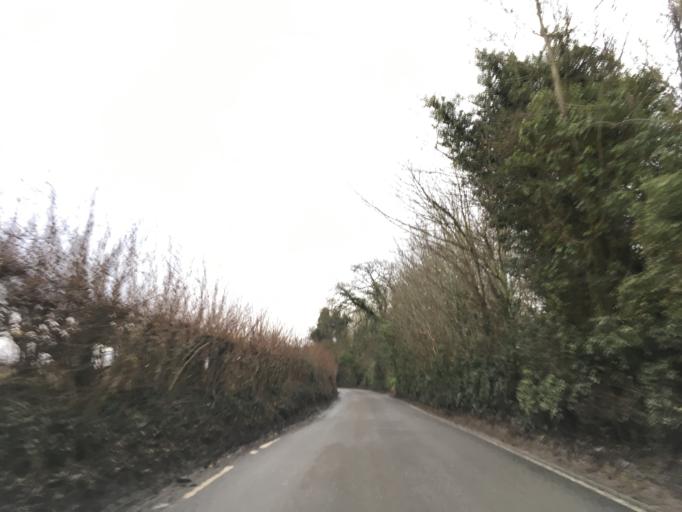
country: GB
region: England
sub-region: South Gloucestershire
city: Winterbourne
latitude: 51.5385
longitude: -2.5210
